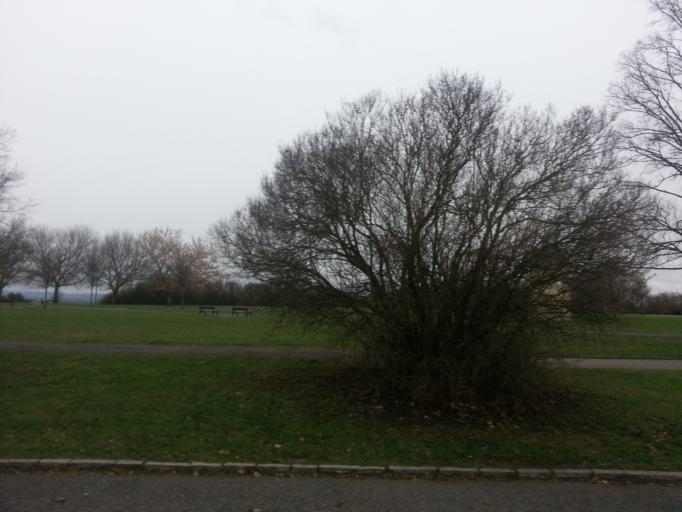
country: CZ
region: Praha
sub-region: Praha 1
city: Mala Strana
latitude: 50.0798
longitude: 14.3582
